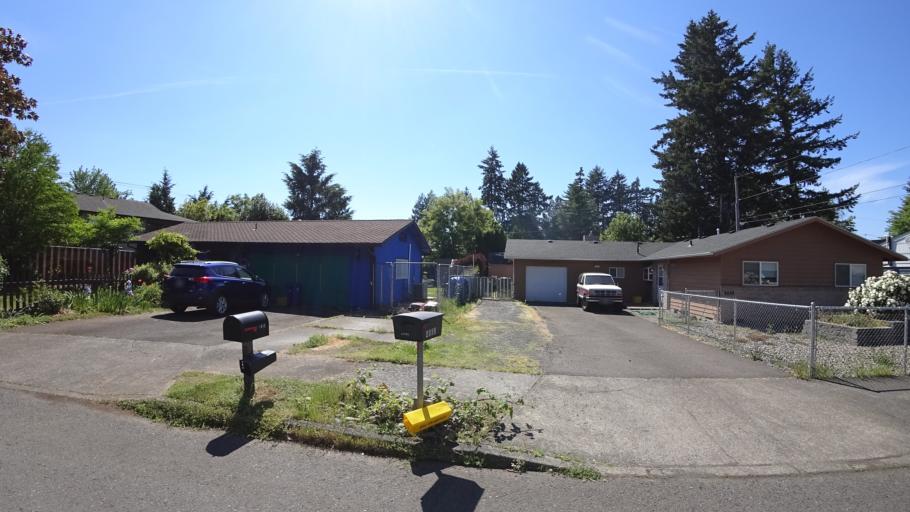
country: US
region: Oregon
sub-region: Multnomah County
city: Gresham
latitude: 45.4934
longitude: -122.4868
